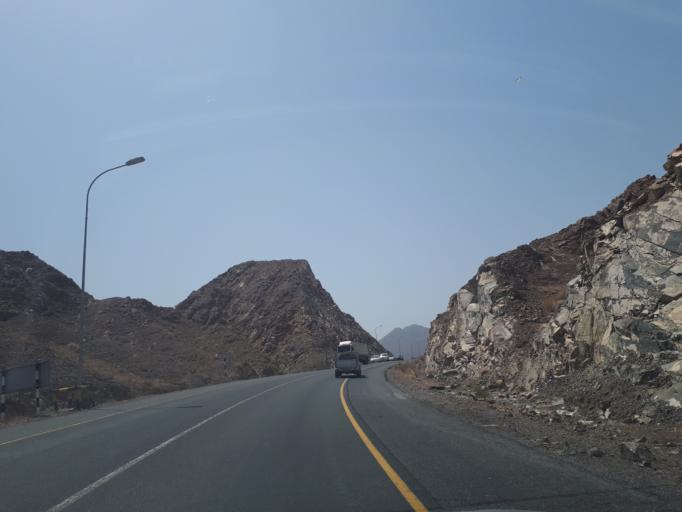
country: OM
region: Muhafazat ad Dakhiliyah
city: Sufalat Sama'il
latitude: 23.1986
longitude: 58.0844
